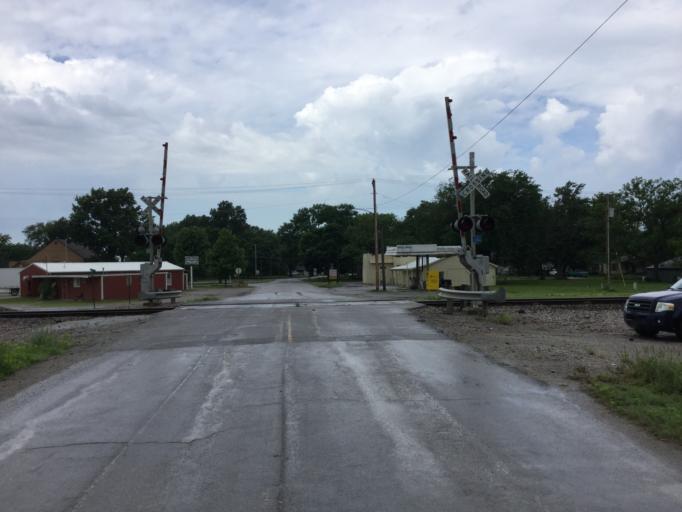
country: US
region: Kansas
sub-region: Linn County
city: Pleasanton
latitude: 38.1805
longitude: -94.7108
